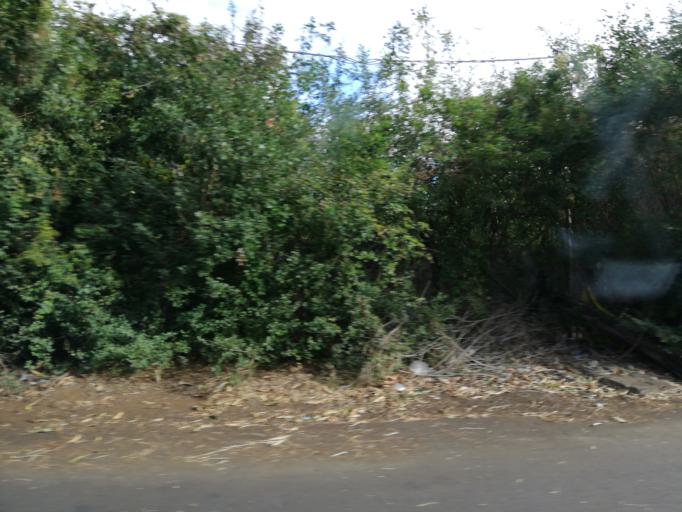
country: MU
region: Black River
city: Petite Riviere
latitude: -20.2252
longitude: 57.4590
